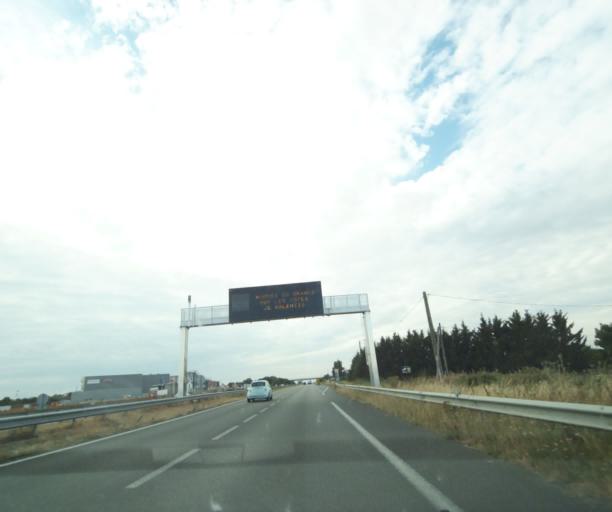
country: FR
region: Poitou-Charentes
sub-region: Departement de la Charente-Maritime
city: Angoulins
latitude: 46.1006
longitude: -1.0926
